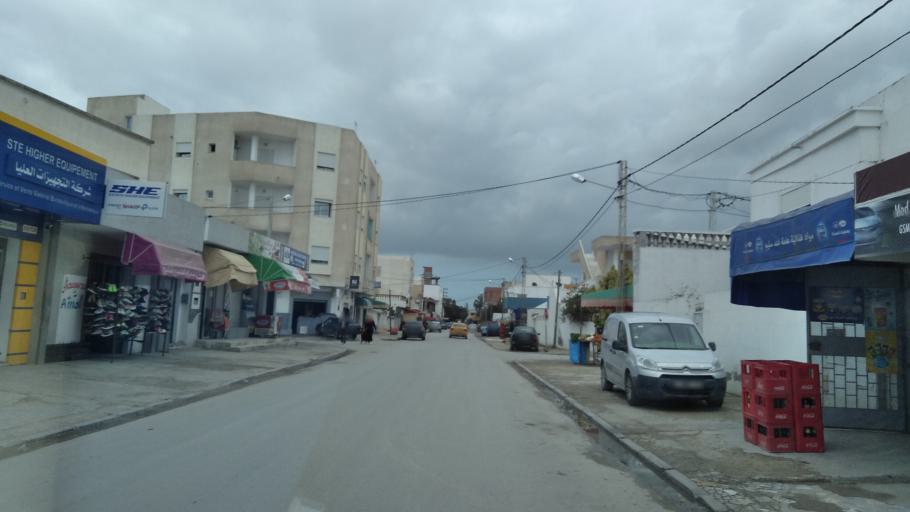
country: TN
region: Bin 'Arus
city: Ben Arous
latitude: 36.7607
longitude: 10.2269
